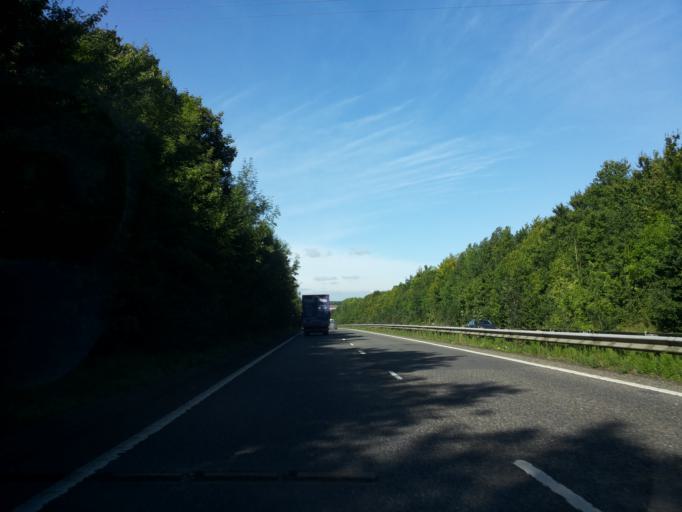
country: GB
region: England
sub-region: Kent
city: Canterbury
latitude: 51.2626
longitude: 1.0719
